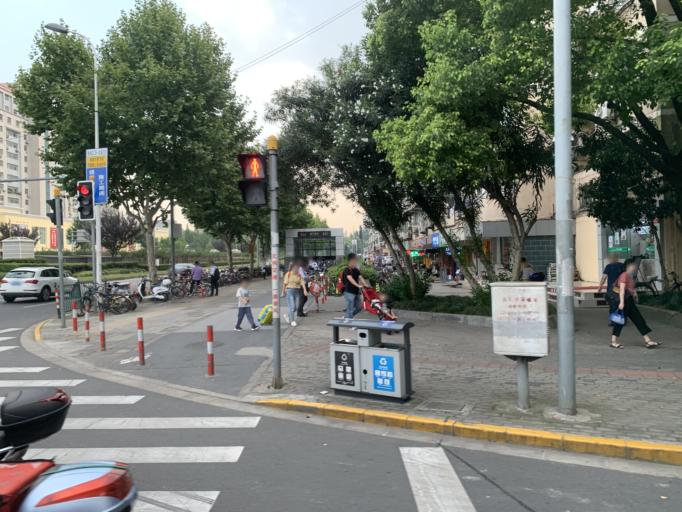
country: CN
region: Shanghai Shi
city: Pudong
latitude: 31.2478
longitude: 121.5608
